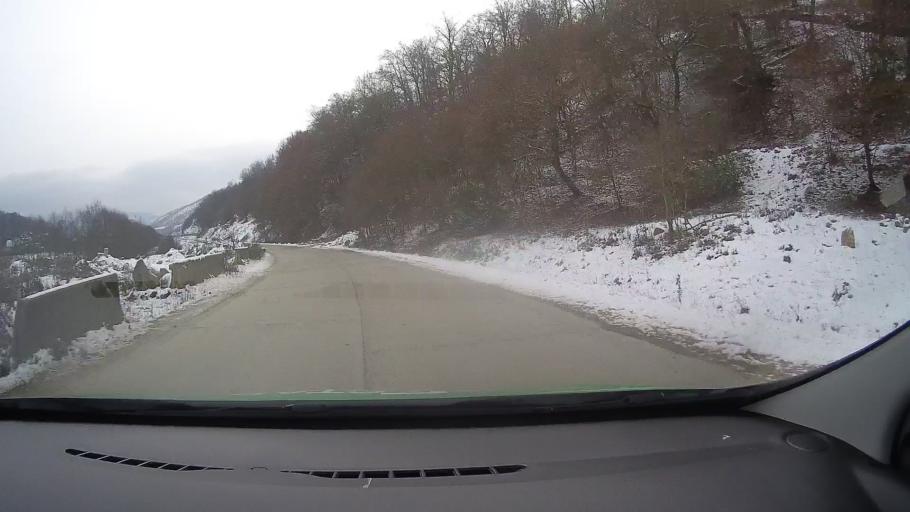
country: RO
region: Alba
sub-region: Oras Zlatna
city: Zlatna
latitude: 46.1177
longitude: 23.2058
